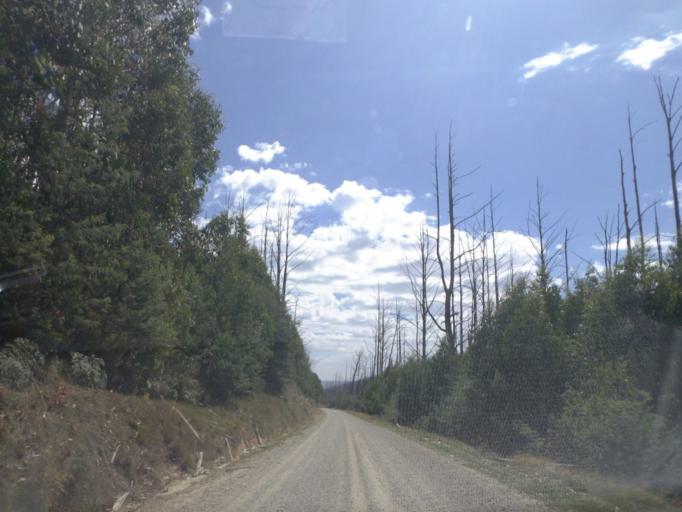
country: AU
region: Victoria
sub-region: Murrindindi
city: Alexandra
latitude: -37.4494
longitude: 145.7938
